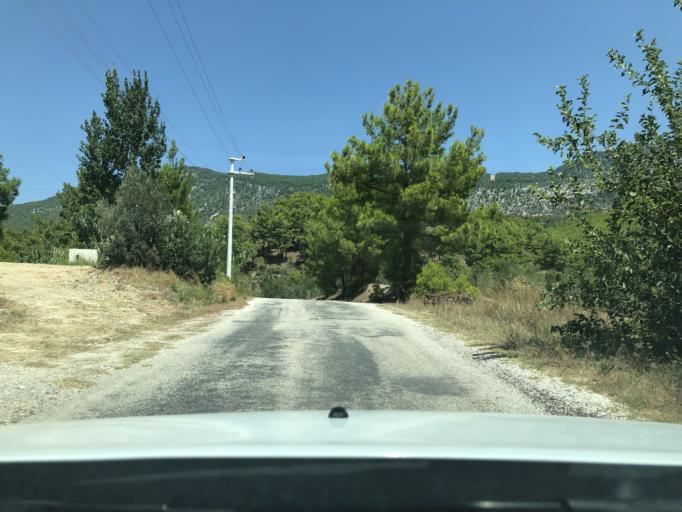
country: TR
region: Antalya
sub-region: Manavgat
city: Kizilagac
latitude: 36.8609
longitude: 31.5639
